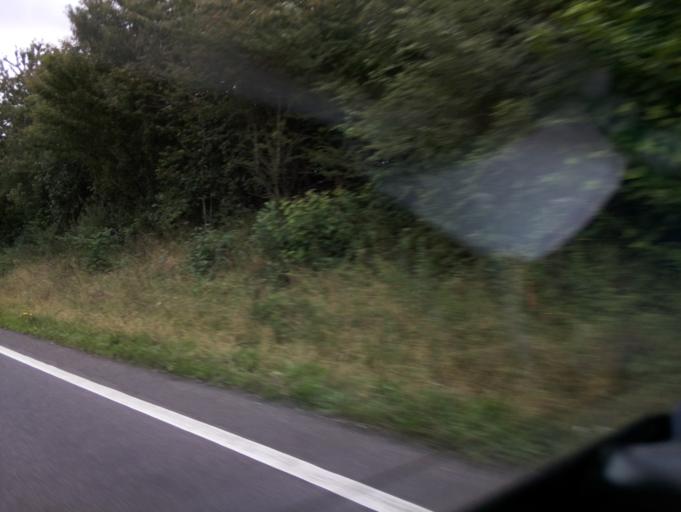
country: GB
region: England
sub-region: Devon
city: Marldon
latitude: 50.4607
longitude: -3.5901
